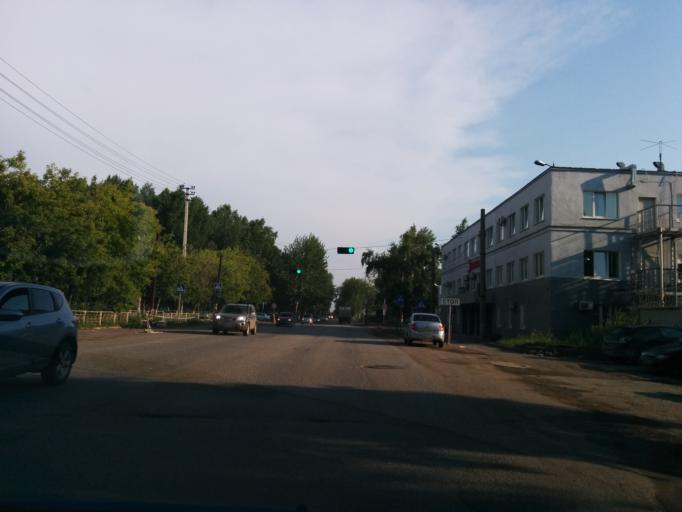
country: RU
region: Perm
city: Perm
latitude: 58.1232
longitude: 56.2928
